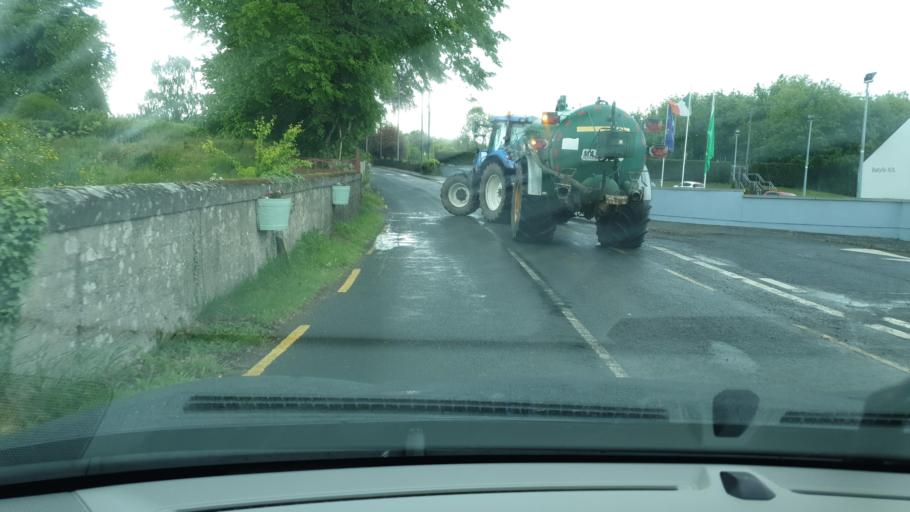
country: IE
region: Leinster
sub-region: Laois
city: Mountrath
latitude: 53.0556
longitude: -7.4075
